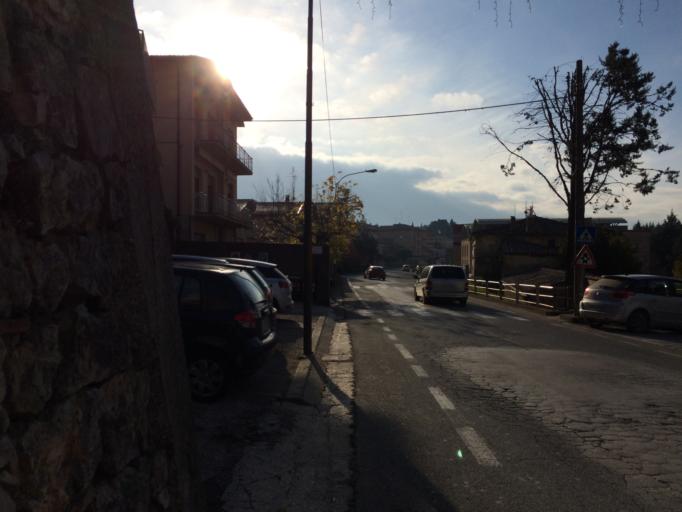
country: IT
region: Umbria
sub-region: Provincia di Terni
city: Amelia
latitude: 42.5513
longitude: 12.4180
